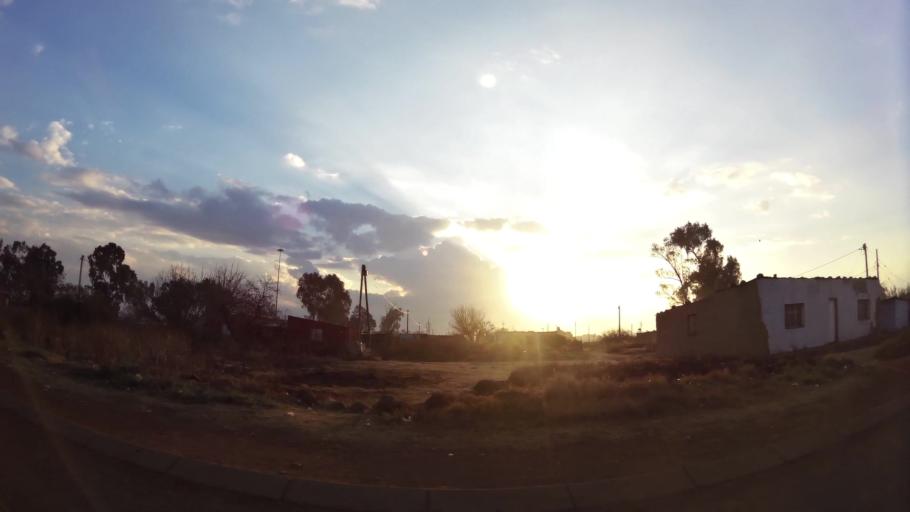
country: ZA
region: Gauteng
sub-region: City of Johannesburg Metropolitan Municipality
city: Orange Farm
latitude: -26.5364
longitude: 27.8506
